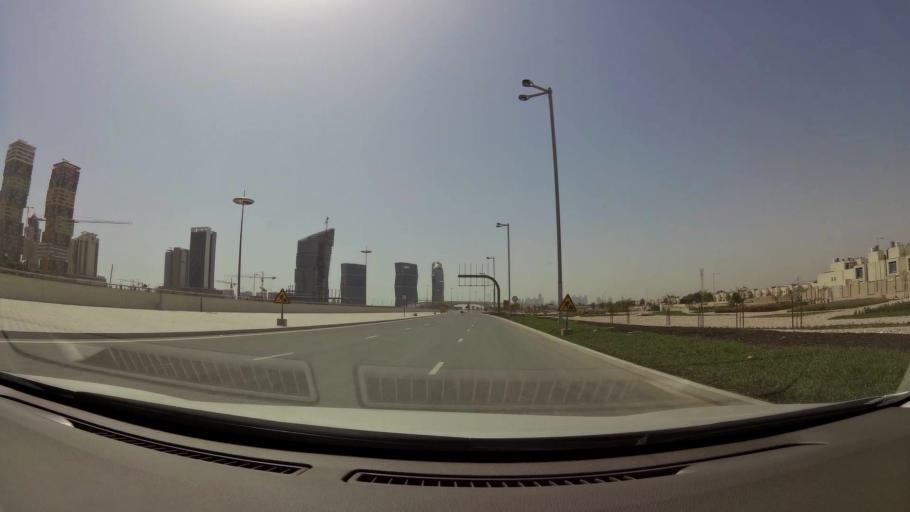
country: QA
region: Baladiyat ad Dawhah
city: Doha
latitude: 25.3881
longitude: 51.5184
